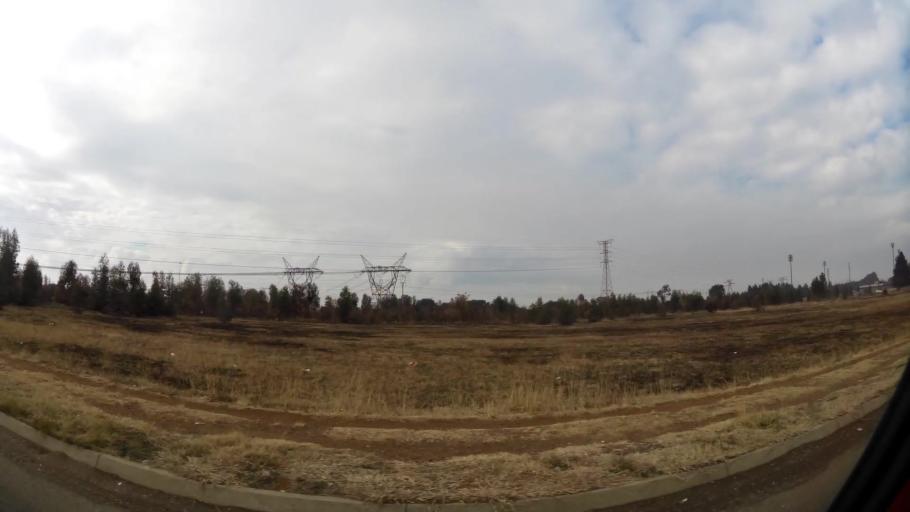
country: ZA
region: Gauteng
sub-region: Sedibeng District Municipality
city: Vanderbijlpark
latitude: -26.6997
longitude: 27.8608
